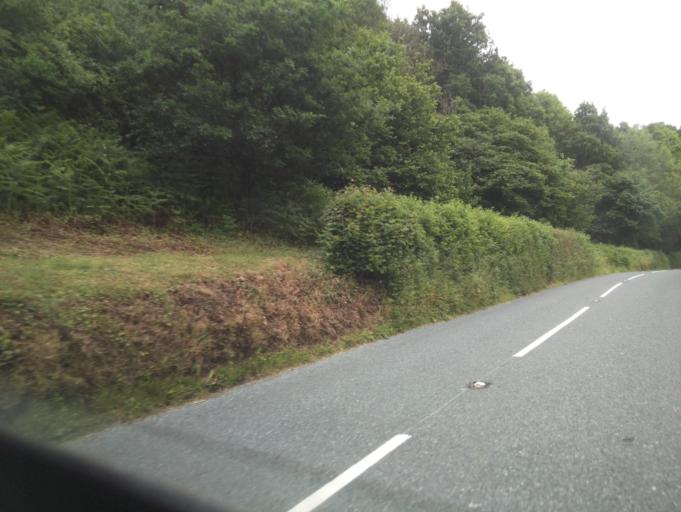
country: GB
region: England
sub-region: Devon
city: Crediton
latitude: 50.6890
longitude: -3.6514
